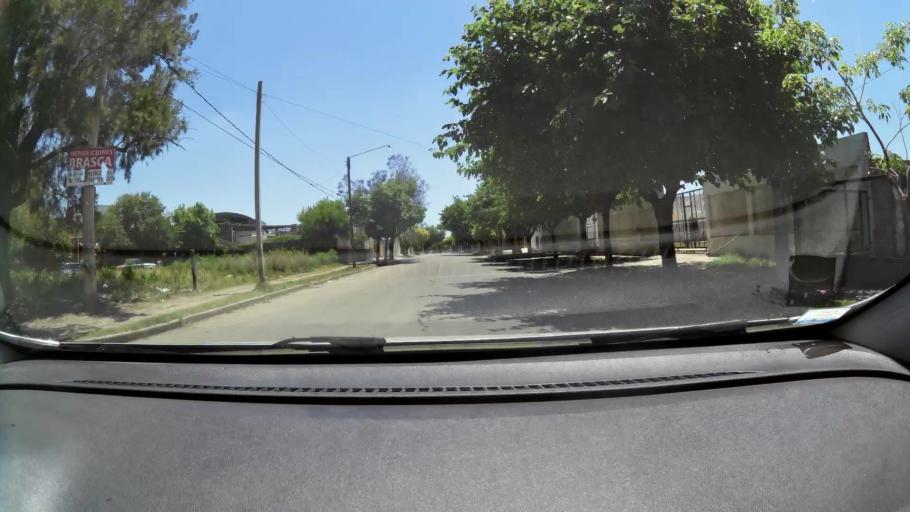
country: AR
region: Cordoba
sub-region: Departamento de Capital
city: Cordoba
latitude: -31.4005
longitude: -64.2084
